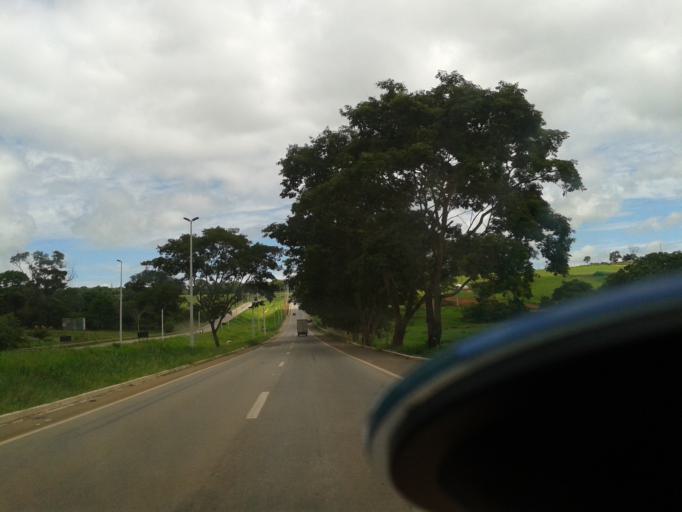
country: BR
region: Goias
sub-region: Inhumas
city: Inhumas
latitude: -16.3502
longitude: -49.5137
